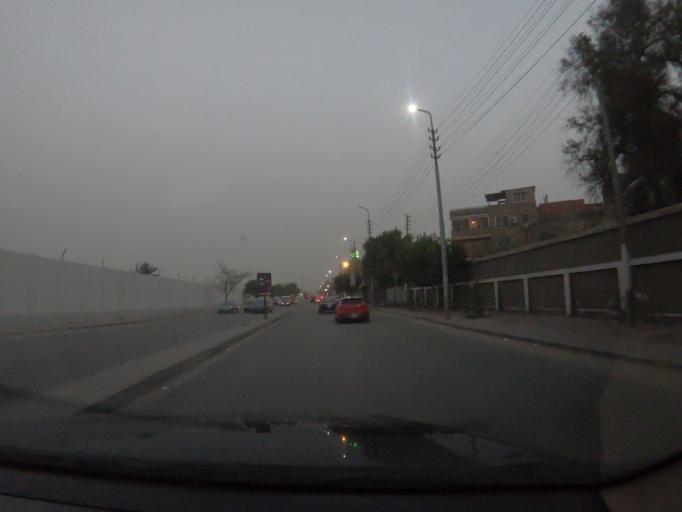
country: EG
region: Muhafazat al Qahirah
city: Cairo
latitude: 30.0876
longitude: 31.3506
